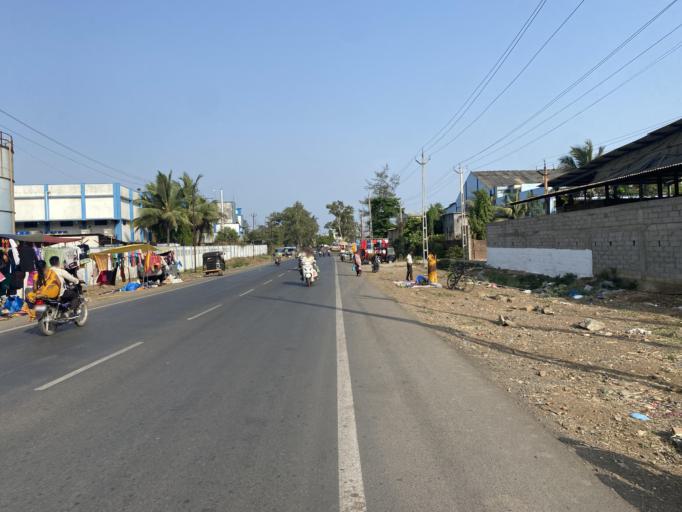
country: IN
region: Gujarat
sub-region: Valsad
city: Vapi
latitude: 20.3031
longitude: 72.8488
